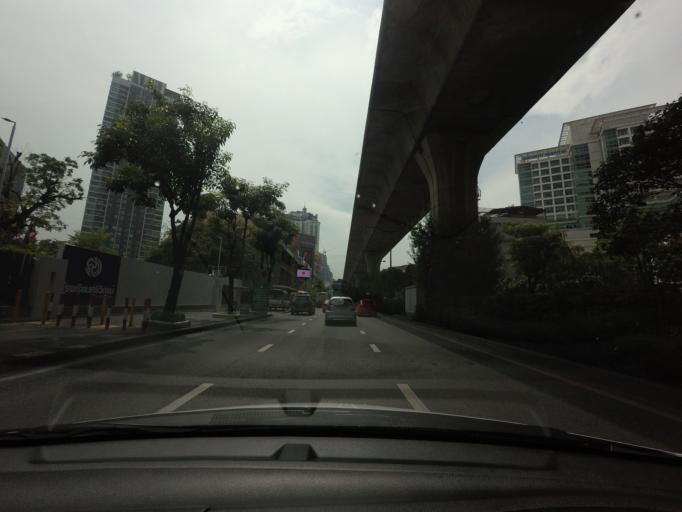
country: TH
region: Bangkok
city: Watthana
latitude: 13.7179
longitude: 100.5873
